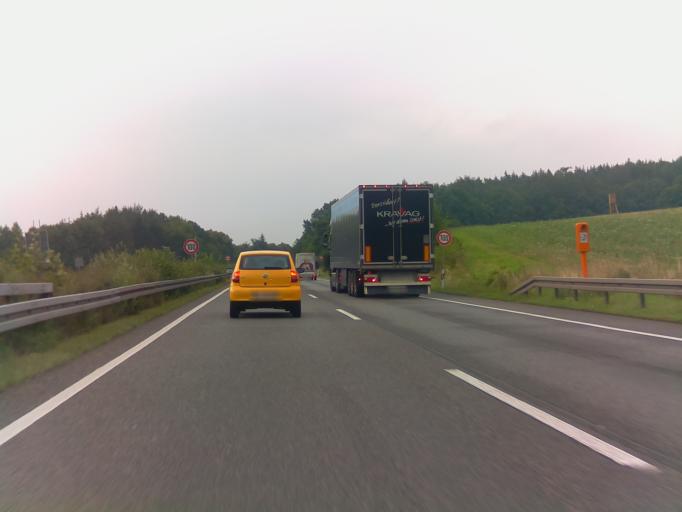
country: DE
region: Hesse
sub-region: Regierungsbezirk Kassel
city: Friedewald
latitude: 50.8752
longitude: 9.7897
